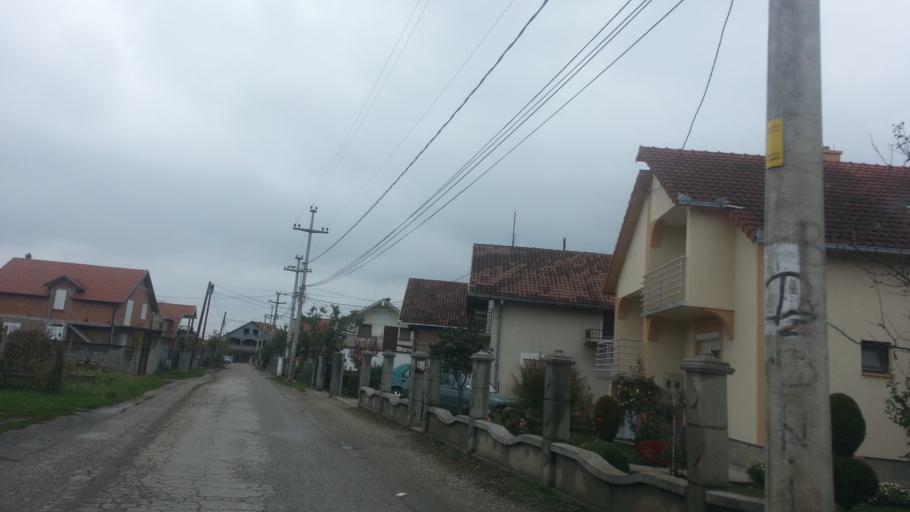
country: RS
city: Novi Banovci
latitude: 44.9167
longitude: 20.2812
